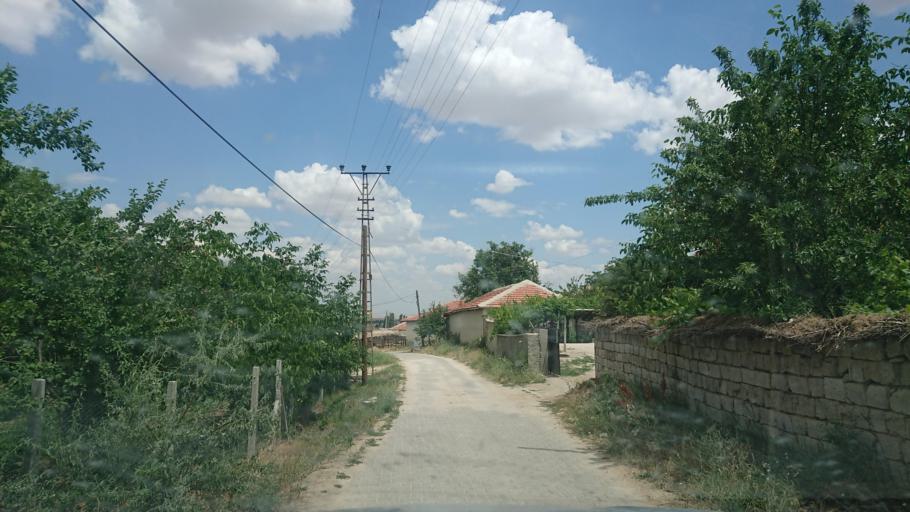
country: TR
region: Aksaray
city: Agacoren
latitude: 38.8864
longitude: 33.8786
